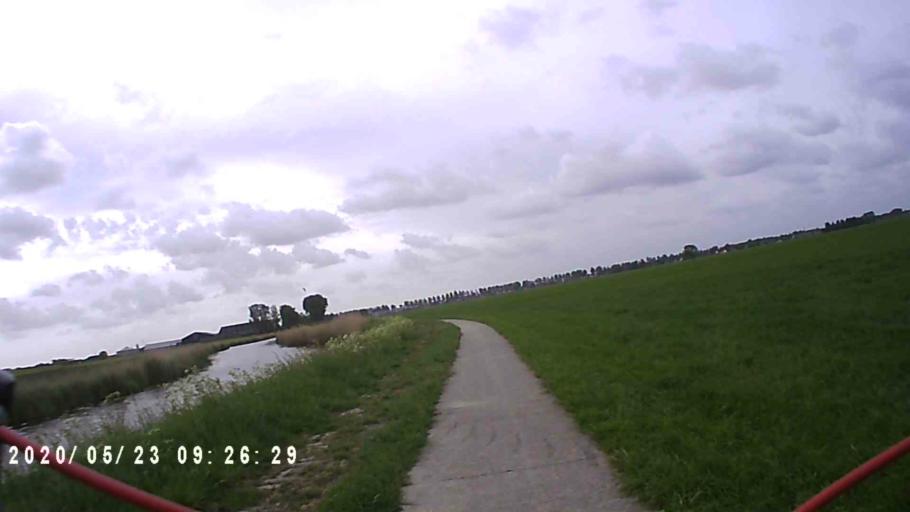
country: NL
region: Groningen
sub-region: Gemeente Bedum
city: Bedum
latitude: 53.2932
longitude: 6.6952
